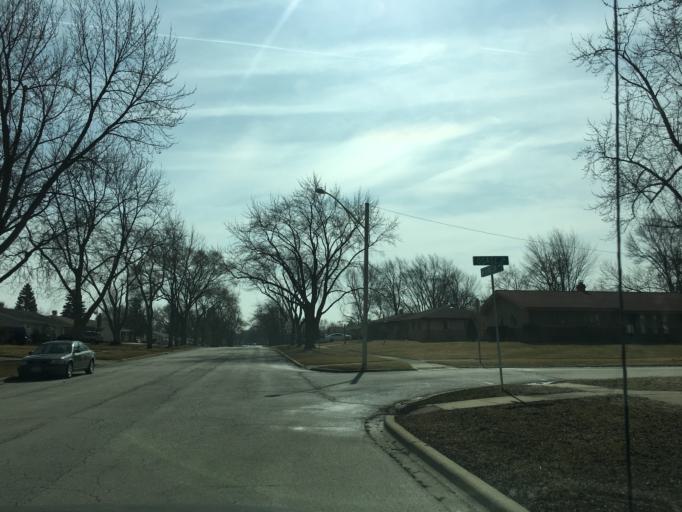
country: US
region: Illinois
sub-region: Cook County
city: Schaumburg
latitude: 42.0302
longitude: -88.0977
